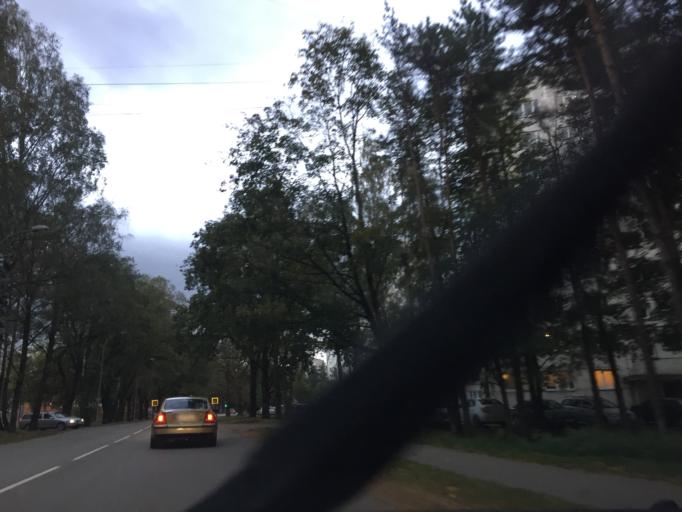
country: LV
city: Tireli
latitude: 56.9545
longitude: 23.6068
